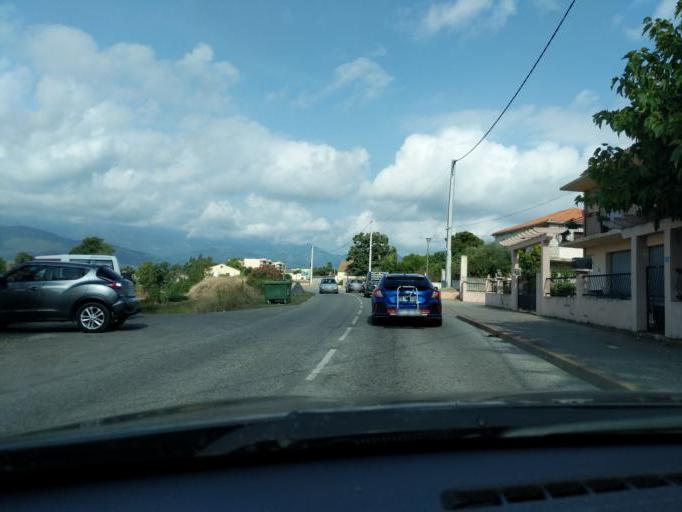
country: FR
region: Corsica
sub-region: Departement de la Haute-Corse
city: Ghisonaccia
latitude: 42.0120
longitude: 9.4095
